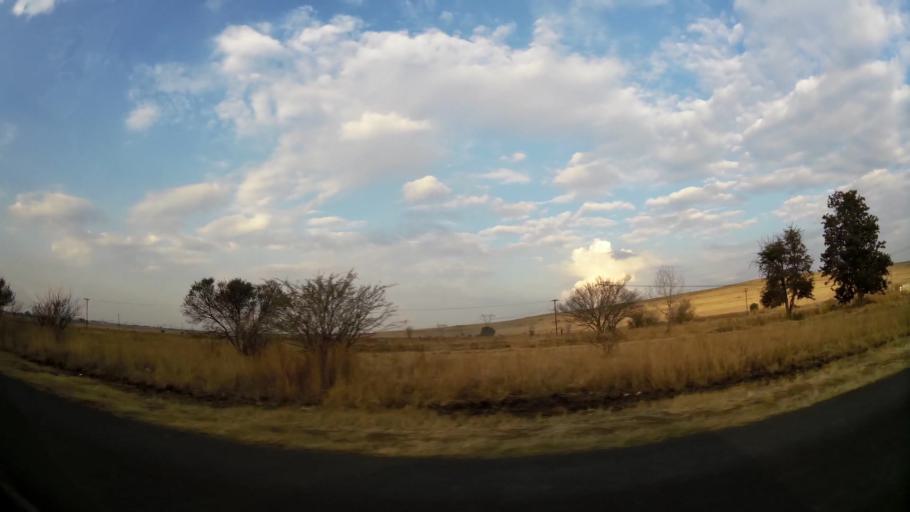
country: ZA
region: Gauteng
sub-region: Sedibeng District Municipality
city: Vanderbijlpark
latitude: -26.6310
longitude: 27.8088
